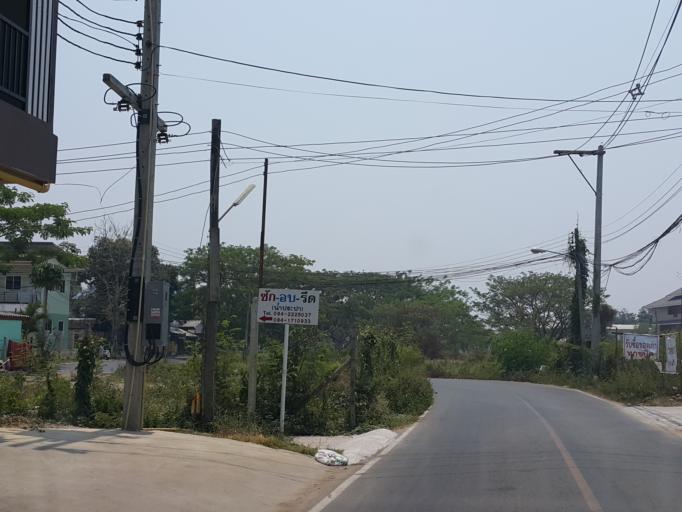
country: TH
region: Chiang Mai
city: Chiang Mai
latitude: 18.7522
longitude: 98.9807
